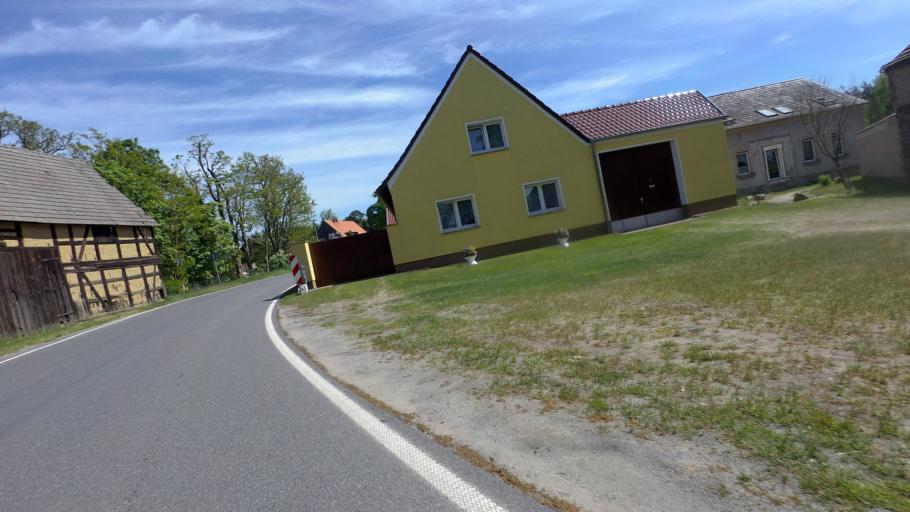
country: DE
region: Brandenburg
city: Sperenberg
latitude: 52.0477
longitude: 13.3916
